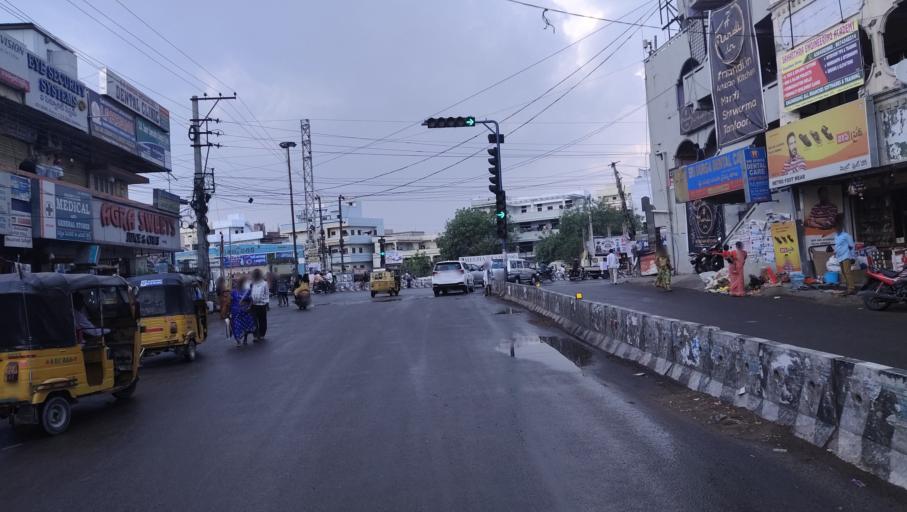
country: IN
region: Telangana
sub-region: Rangareddi
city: Lal Bahadur Nagar
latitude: 17.3208
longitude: 78.5609
